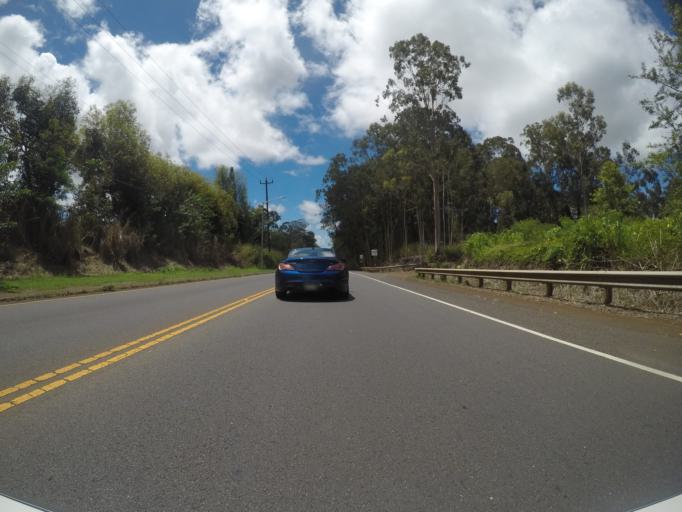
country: US
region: Hawaii
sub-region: Honolulu County
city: Schofield Barracks
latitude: 21.4976
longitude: -158.0512
